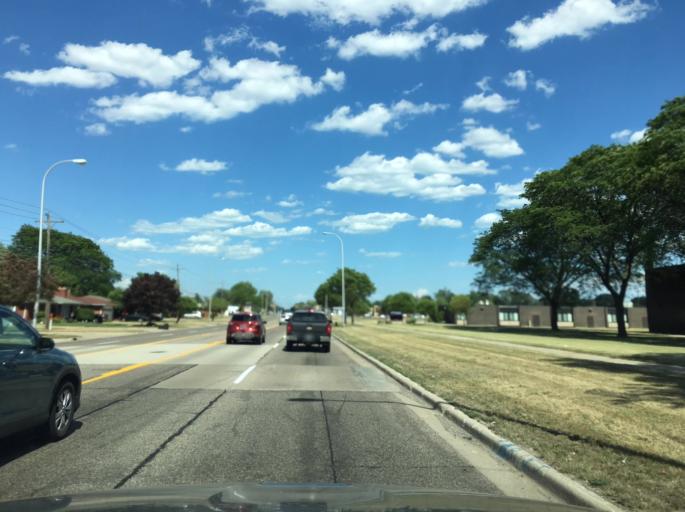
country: US
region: Michigan
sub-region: Macomb County
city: Center Line
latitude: 42.5075
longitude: -82.9917
